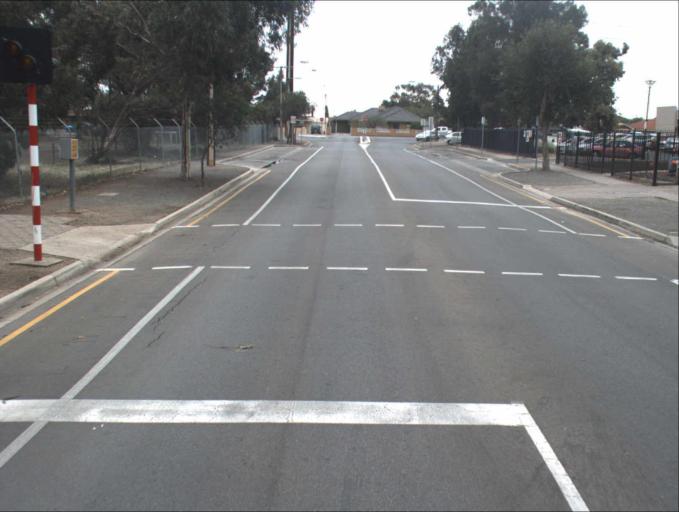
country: AU
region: South Australia
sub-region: Port Adelaide Enfield
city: Gilles Plains
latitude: -34.8471
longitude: 138.6533
